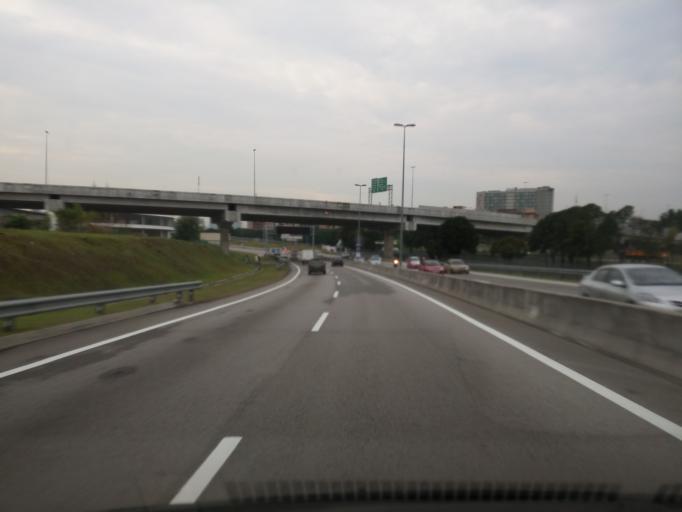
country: MY
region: Kuala Lumpur
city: Kuala Lumpur
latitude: 3.1171
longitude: 101.7163
